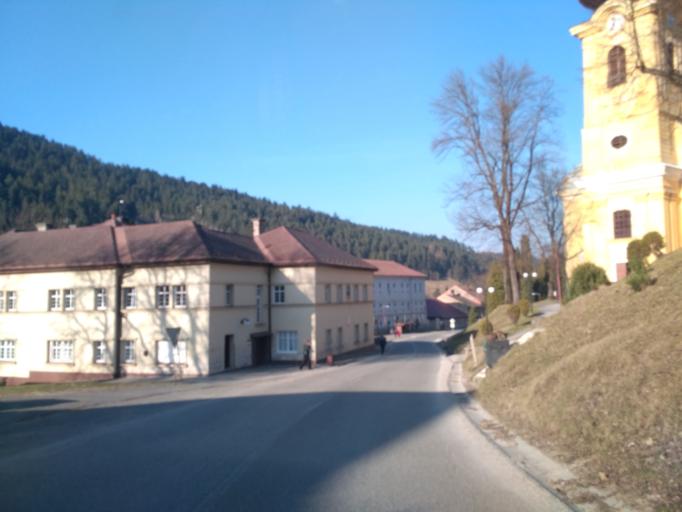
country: SK
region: Kosicky
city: Medzev
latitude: 48.7292
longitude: 20.7390
